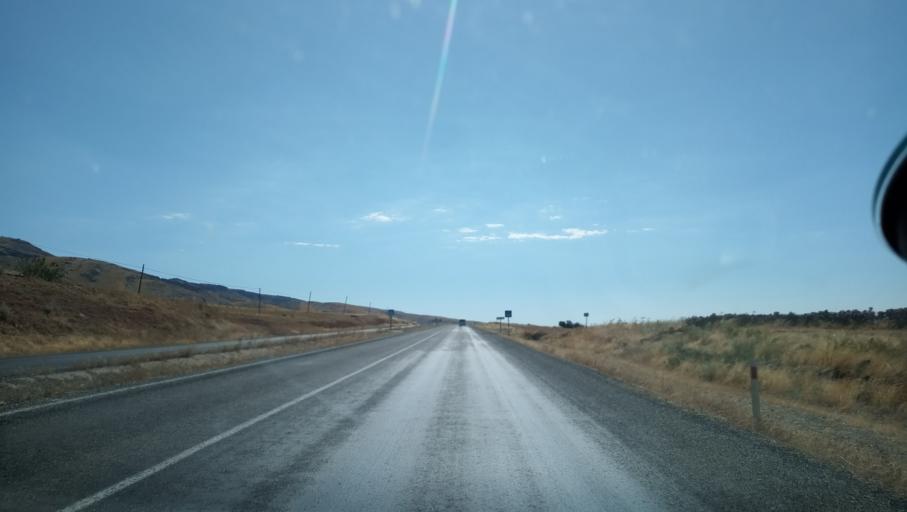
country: TR
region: Diyarbakir
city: Silvan
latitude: 38.1279
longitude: 41.0655
